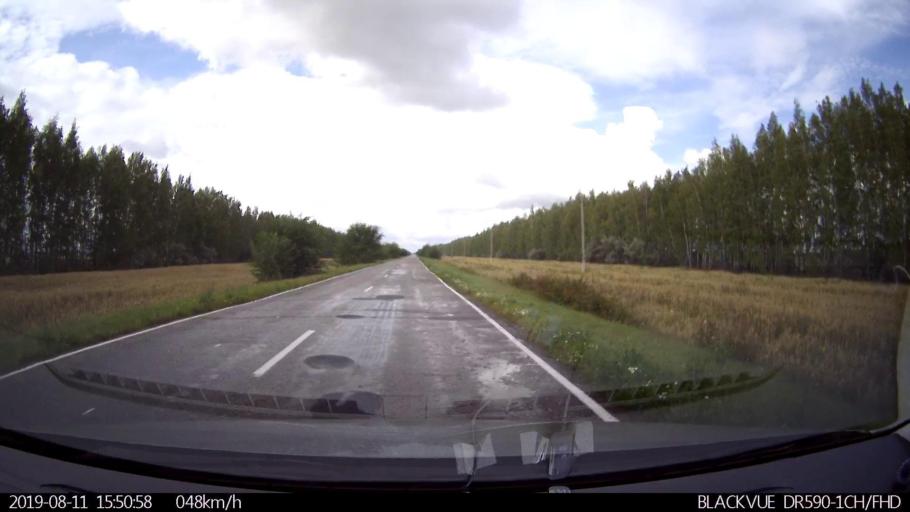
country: RU
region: Ulyanovsk
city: Ignatovka
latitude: 53.9153
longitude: 47.6559
